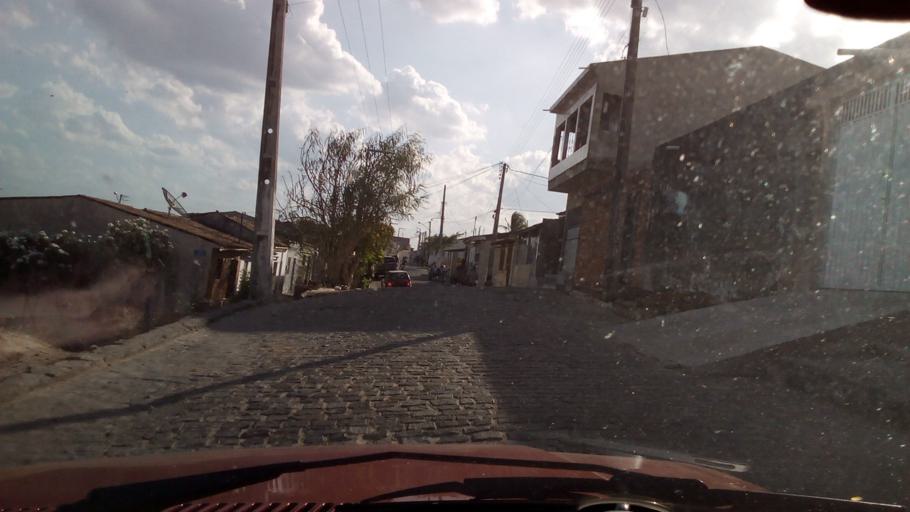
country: BR
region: Paraiba
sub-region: Arara
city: Arara
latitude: -6.8351
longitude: -35.7637
